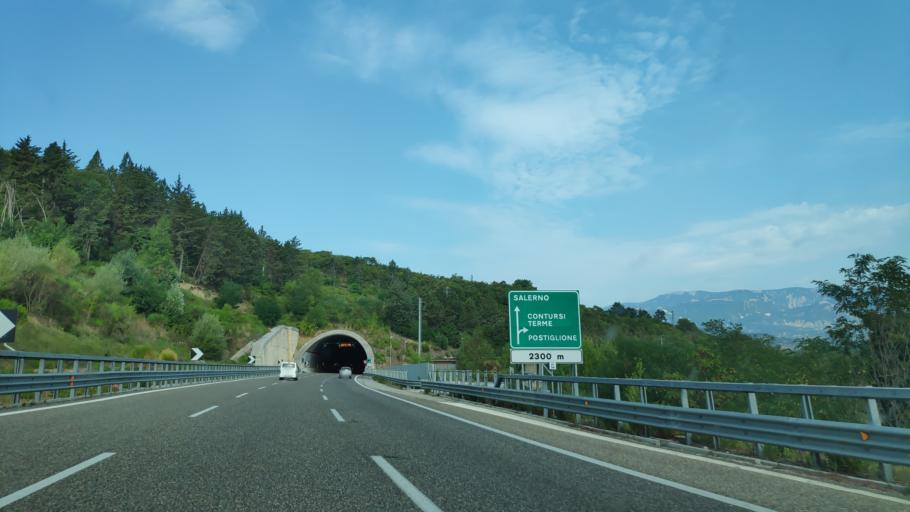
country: IT
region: Campania
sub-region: Provincia di Salerno
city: Contursi Terme
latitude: 40.6130
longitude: 15.2523
